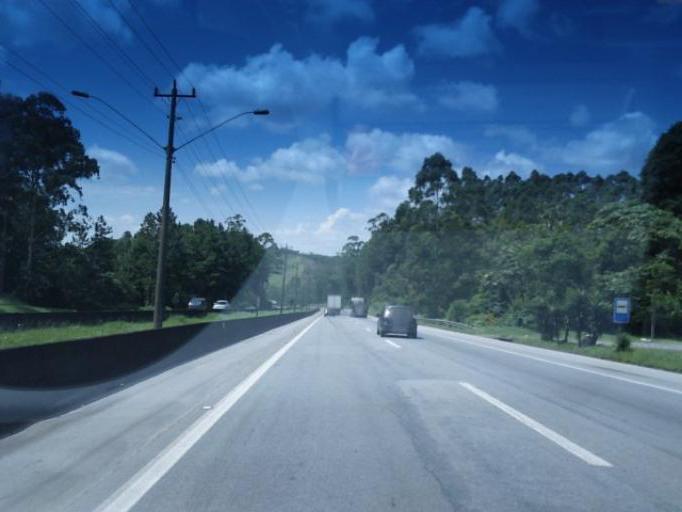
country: BR
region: Sao Paulo
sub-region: Sao Lourenco Da Serra
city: Sao Lourenco da Serra
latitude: -23.7916
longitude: -46.9149
